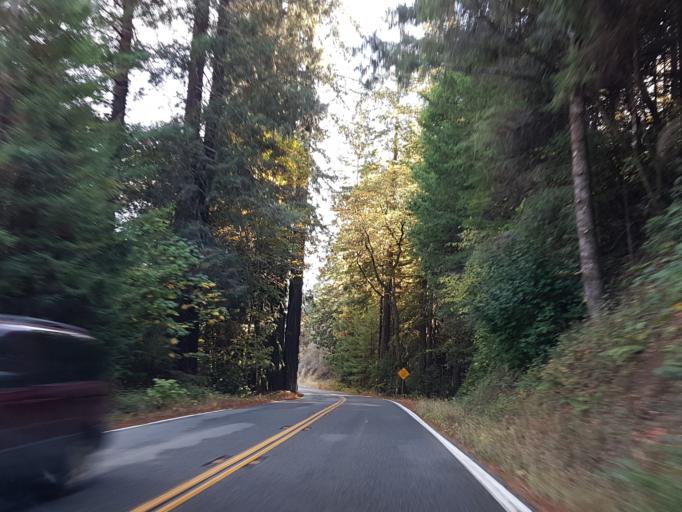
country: US
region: California
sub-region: Humboldt County
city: Rio Dell
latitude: 40.4278
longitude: -123.9825
